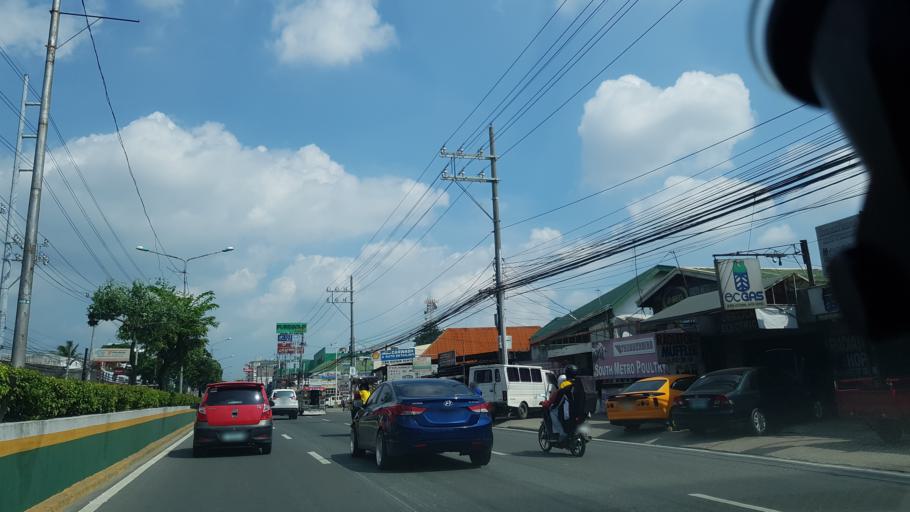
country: PH
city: Sambayanihan People's Village
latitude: 14.4675
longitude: 121.0145
